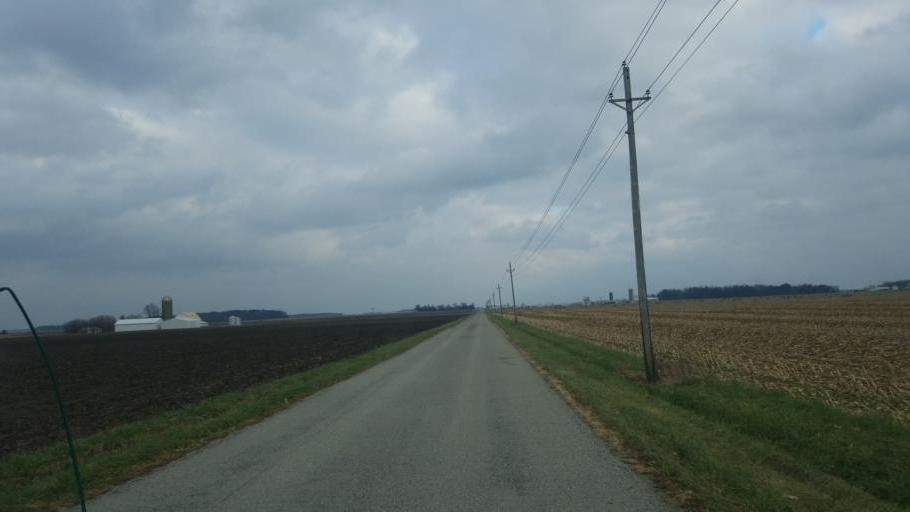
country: US
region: Ohio
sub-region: Mercer County
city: Fort Recovery
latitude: 40.5135
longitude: -84.8548
